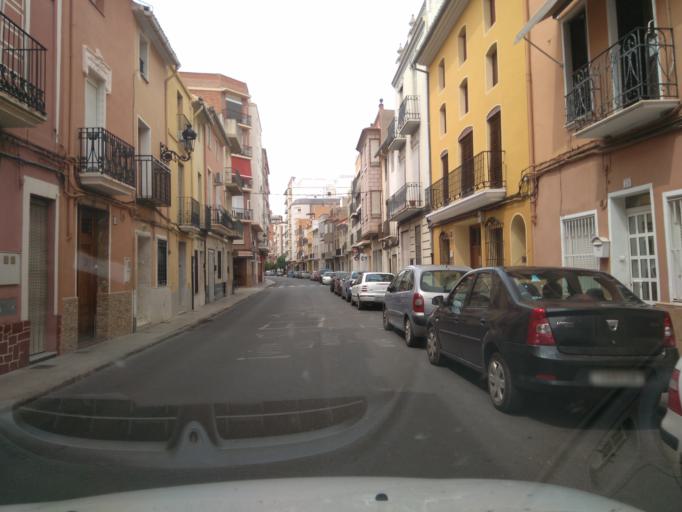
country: ES
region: Valencia
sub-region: Provincia de Valencia
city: Carcaixent
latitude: 39.1199
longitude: -0.4456
